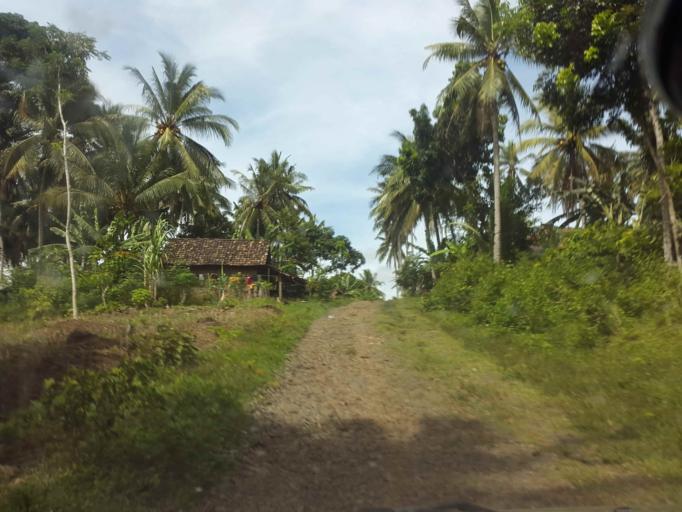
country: ID
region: Lampung
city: Sidorejo
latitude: -5.6275
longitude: 105.4586
